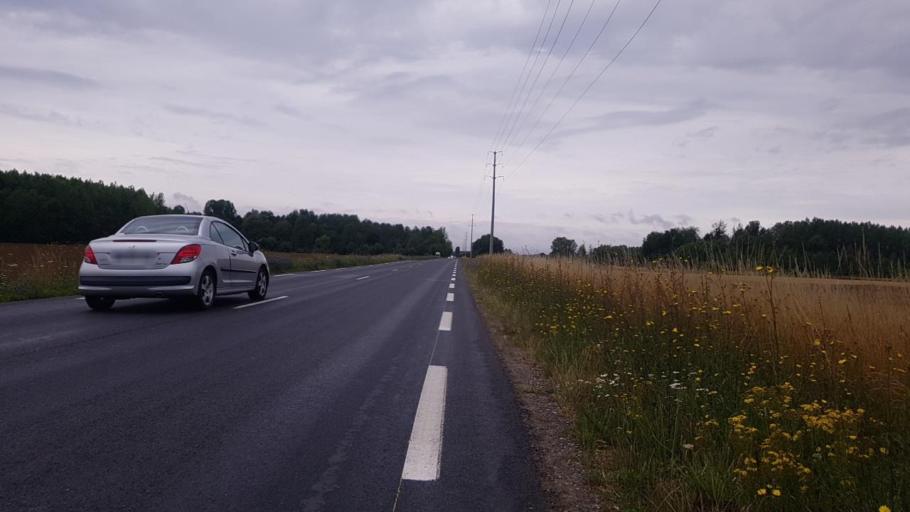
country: FR
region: Champagne-Ardenne
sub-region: Departement de la Marne
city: Vitry-le-Francois
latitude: 48.7413
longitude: 4.6535
